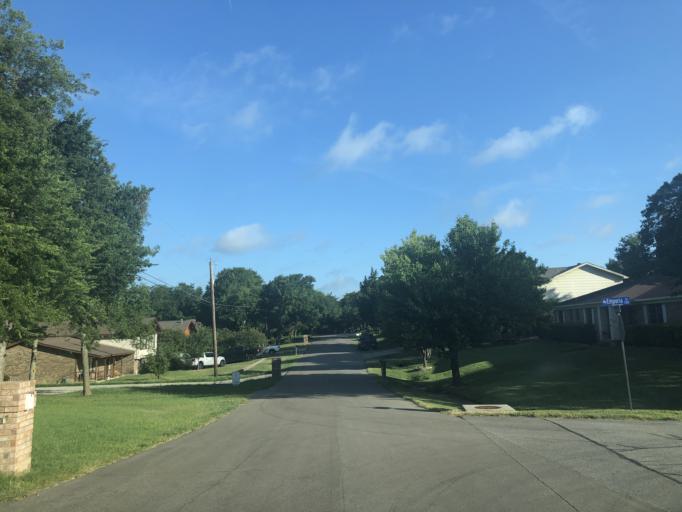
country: US
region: Texas
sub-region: Dallas County
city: Duncanville
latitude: 32.6698
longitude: -96.9114
